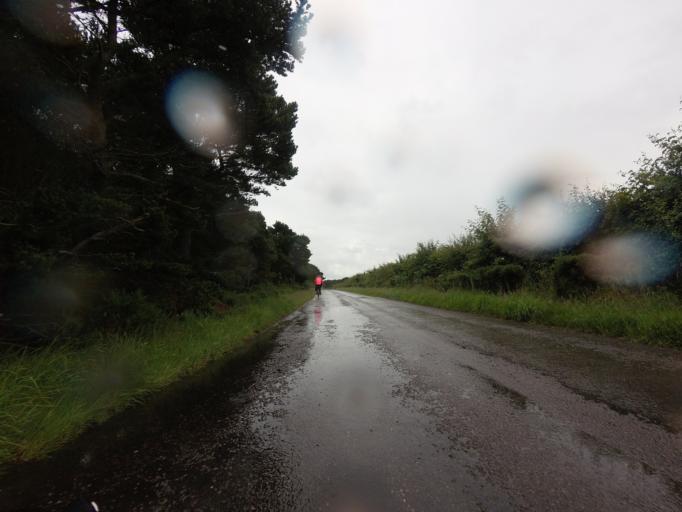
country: GB
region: Scotland
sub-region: Moray
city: Fochabers
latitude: 57.6659
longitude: -3.0761
